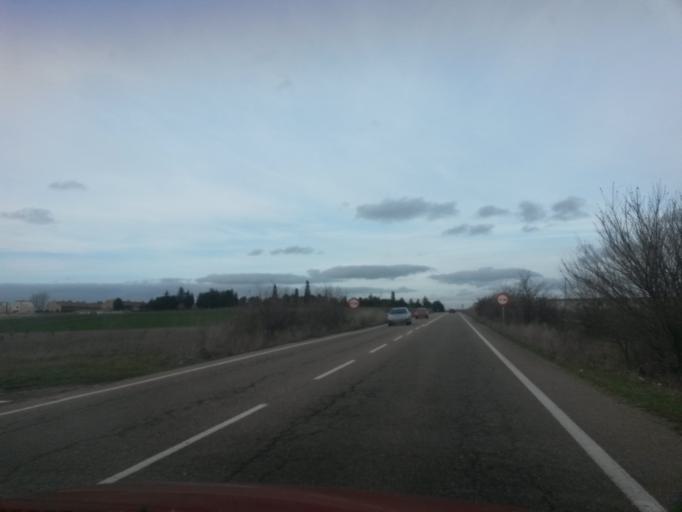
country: ES
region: Castille and Leon
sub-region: Provincia de Salamanca
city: Salamanca
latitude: 40.9888
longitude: -5.6590
